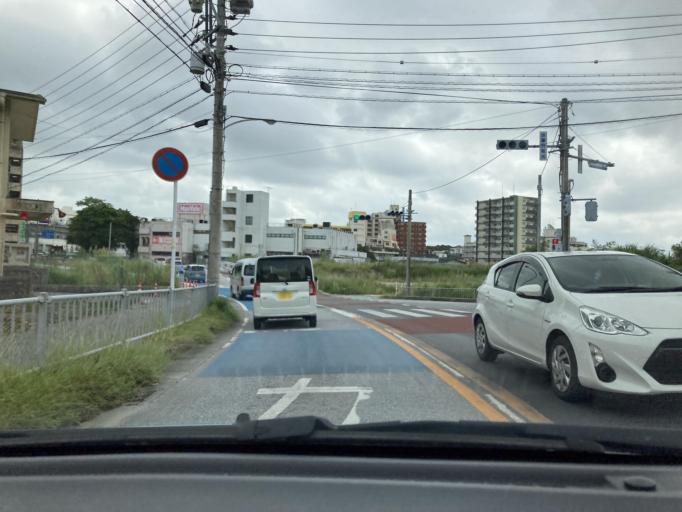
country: JP
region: Okinawa
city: Ginowan
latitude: 26.2403
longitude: 127.7493
